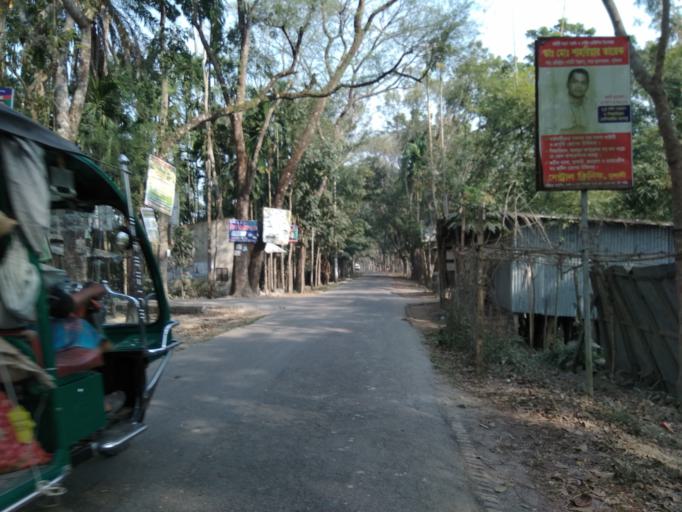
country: BD
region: Barisal
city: Mehendiganj
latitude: 22.9590
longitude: 90.4150
